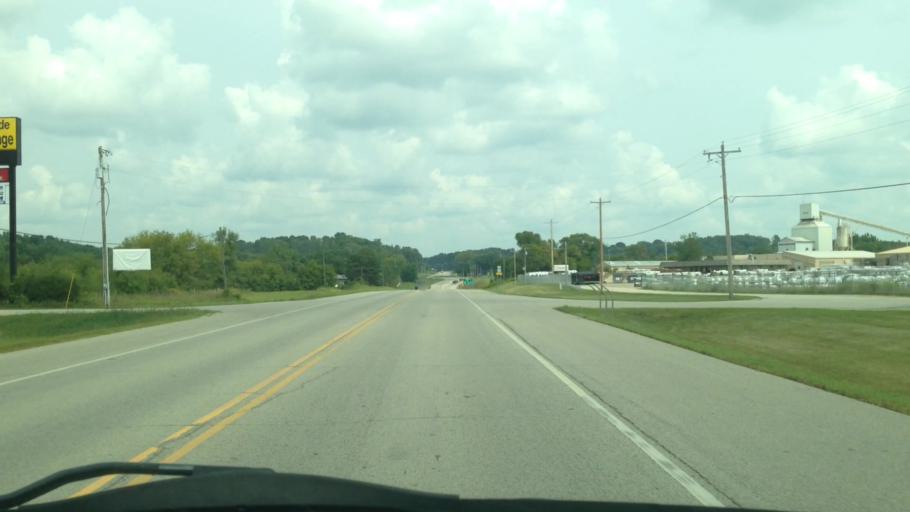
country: US
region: Minnesota
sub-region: Olmsted County
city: Rochester
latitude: 44.1017
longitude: -92.4355
